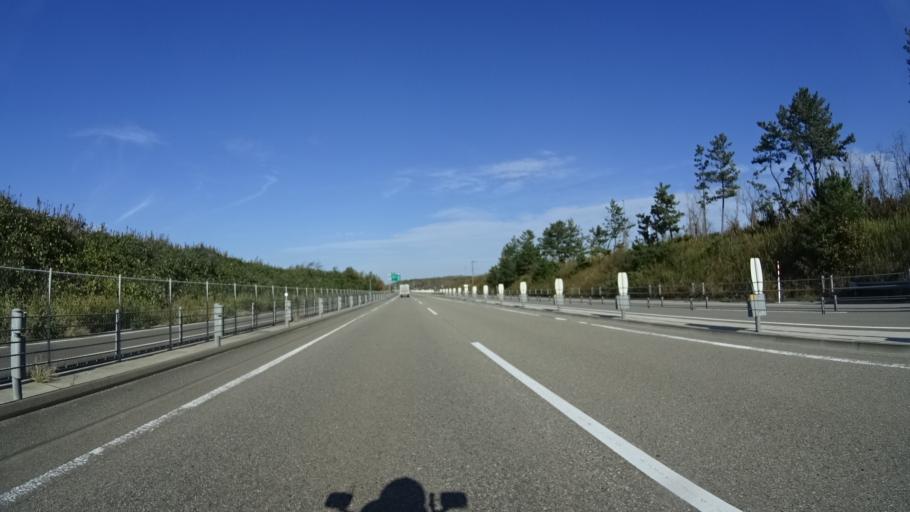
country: JP
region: Ishikawa
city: Kanazawa-shi
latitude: 36.6605
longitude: 136.6421
